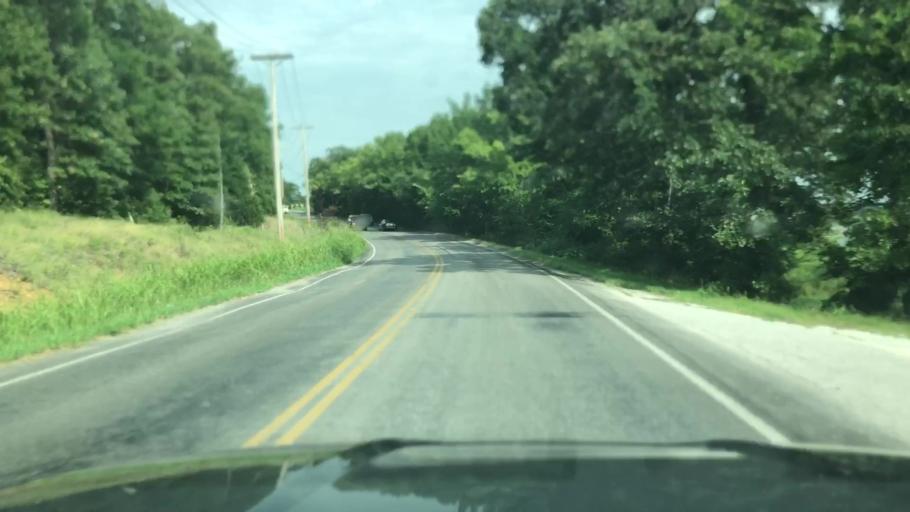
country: US
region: Oklahoma
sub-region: Tulsa County
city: Oakhurst
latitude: 36.0899
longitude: -96.0781
